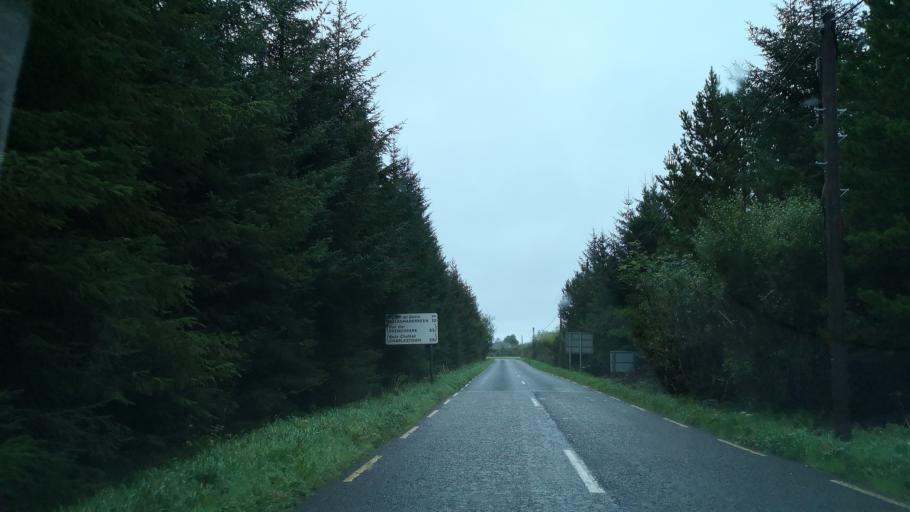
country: IE
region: Connaught
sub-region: Roscommon
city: Ballaghaderreen
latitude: 53.8216
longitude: -8.6225
